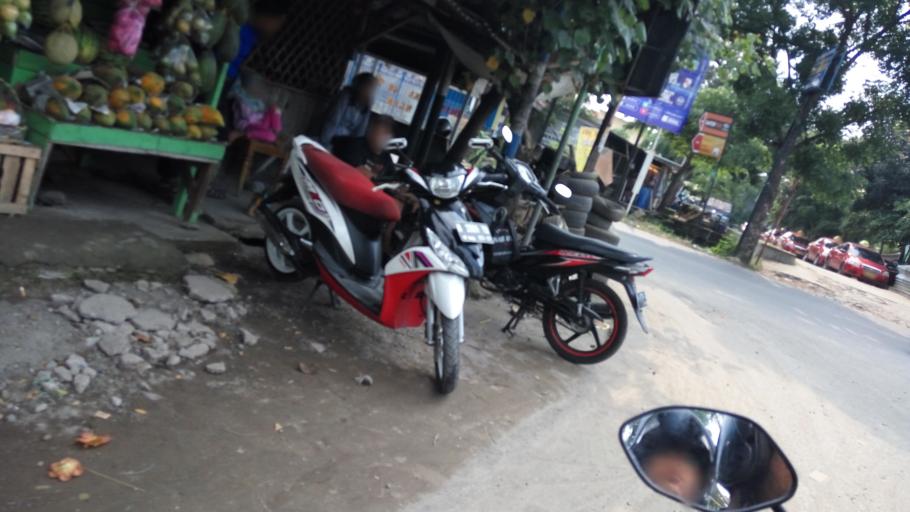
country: ID
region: Central Java
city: Mranggen
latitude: -7.0353
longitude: 110.4676
